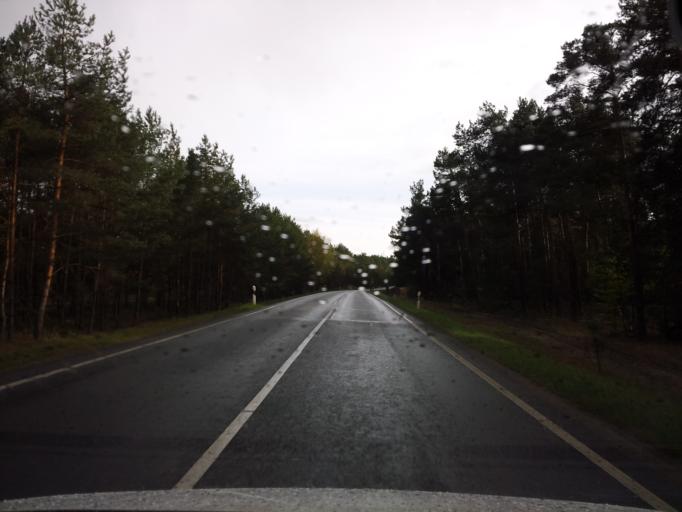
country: DE
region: Brandenburg
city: Heinersbruck
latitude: 51.7461
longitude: 14.4630
